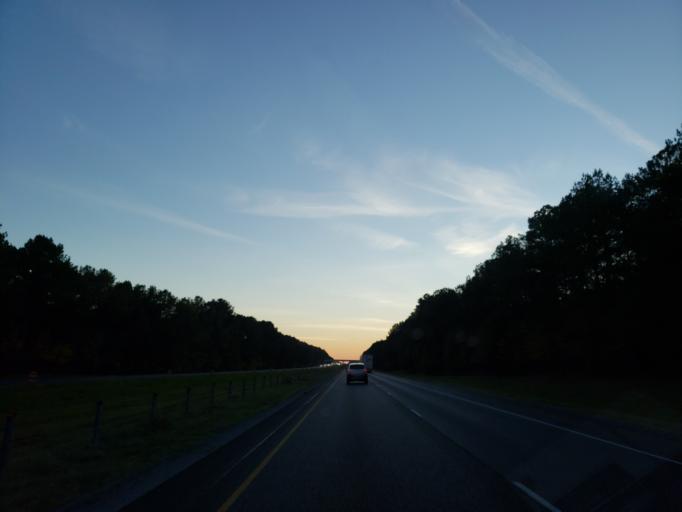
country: US
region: Alabama
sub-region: Sumter County
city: Livingston
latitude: 32.5610
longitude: -88.2597
